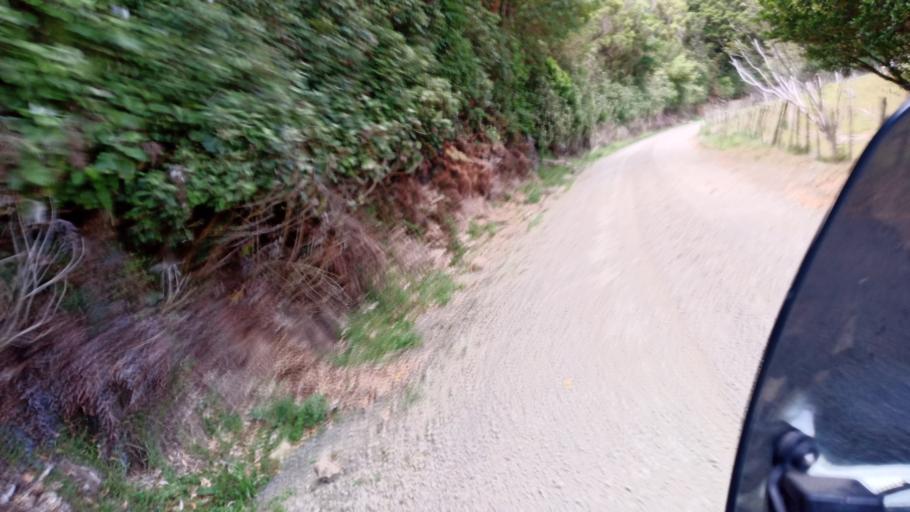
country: NZ
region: Gisborne
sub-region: Gisborne District
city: Gisborne
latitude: -38.4631
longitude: 177.5365
